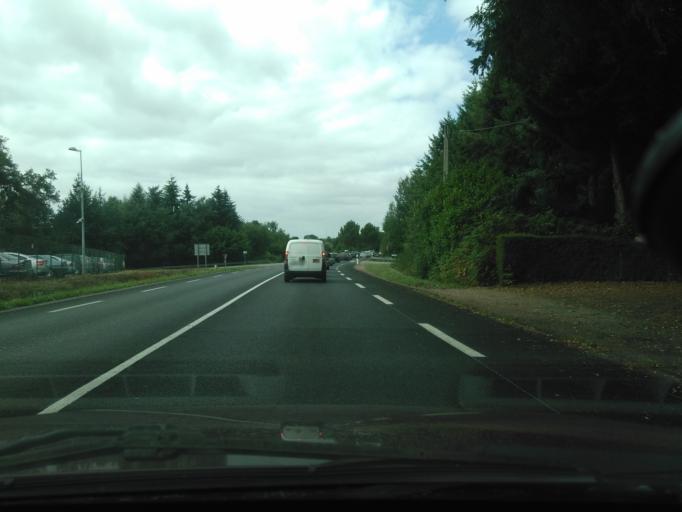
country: FR
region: Pays de la Loire
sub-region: Departement de la Vendee
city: La Roche-sur-Yon
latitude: 46.6802
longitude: -1.3946
